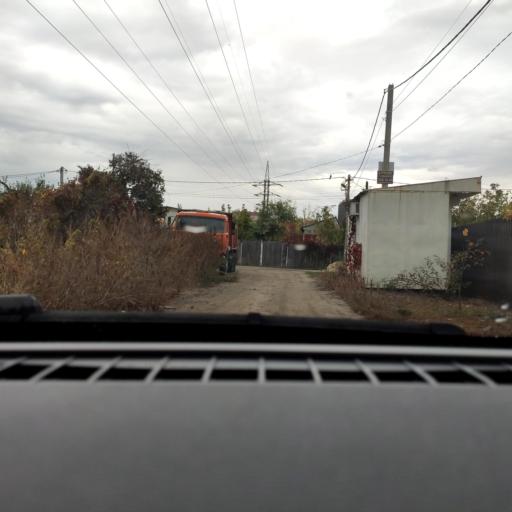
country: RU
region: Voronezj
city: Maslovka
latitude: 51.6029
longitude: 39.2324
